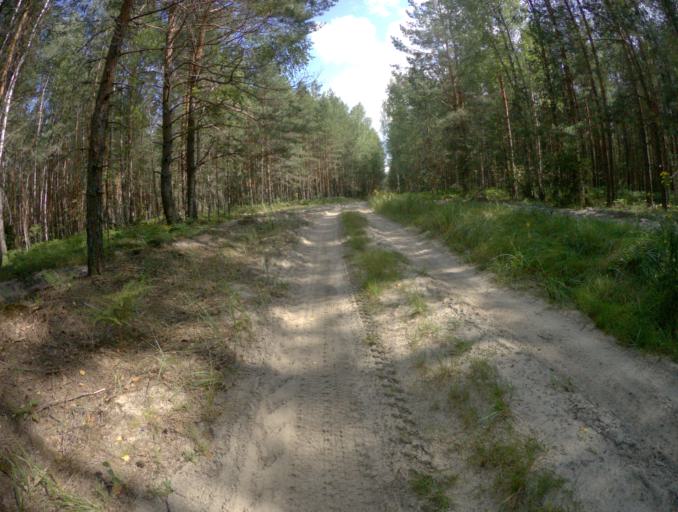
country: RU
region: Vladimir
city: Vorsha
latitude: 55.9192
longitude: 40.1494
